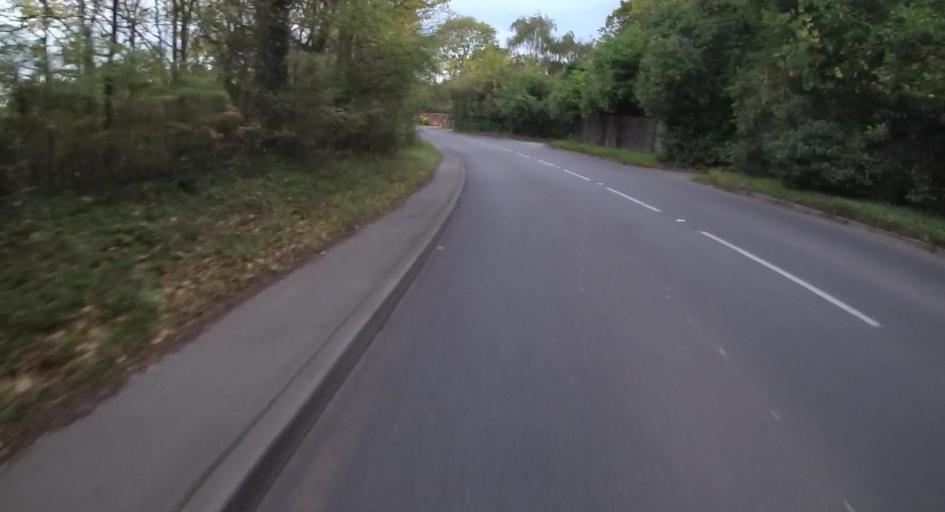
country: GB
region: England
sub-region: Wokingham
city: Finchampstead
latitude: 51.3653
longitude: -0.8550
